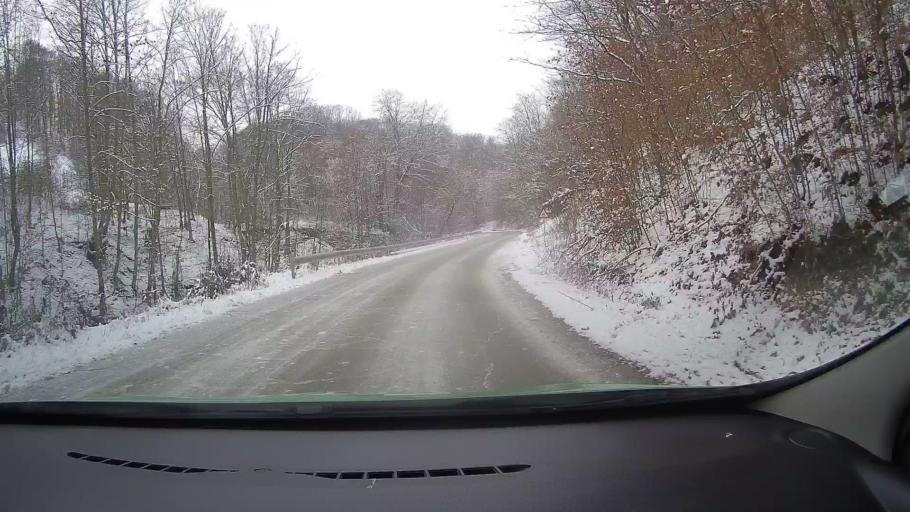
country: RO
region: Alba
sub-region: Oras Zlatna
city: Zlatna
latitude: 46.0961
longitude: 23.1778
